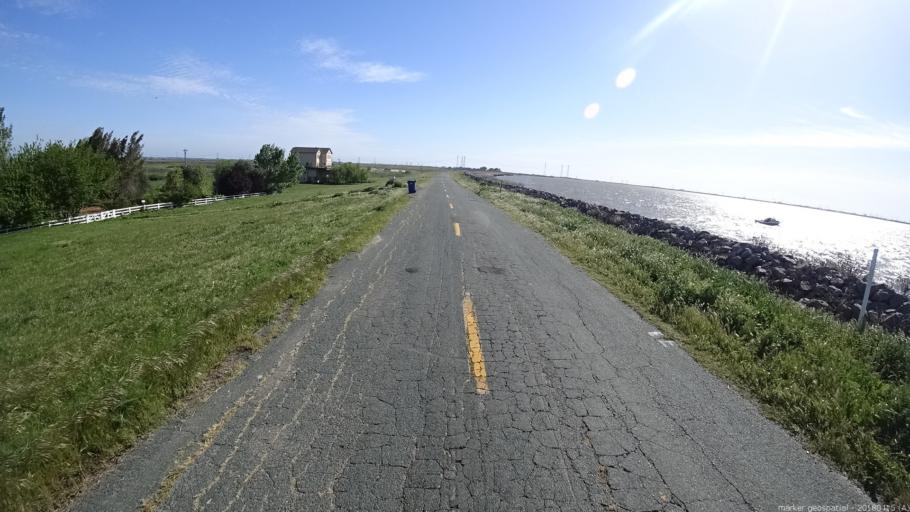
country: US
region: California
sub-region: Contra Costa County
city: Oakley
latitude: 38.0426
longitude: -121.7203
